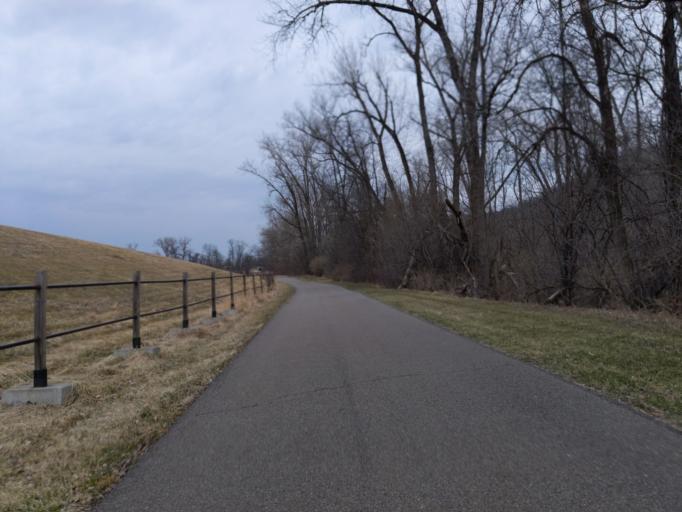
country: US
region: New York
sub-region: Chemung County
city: Elmira
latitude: 42.0920
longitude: -76.7851
